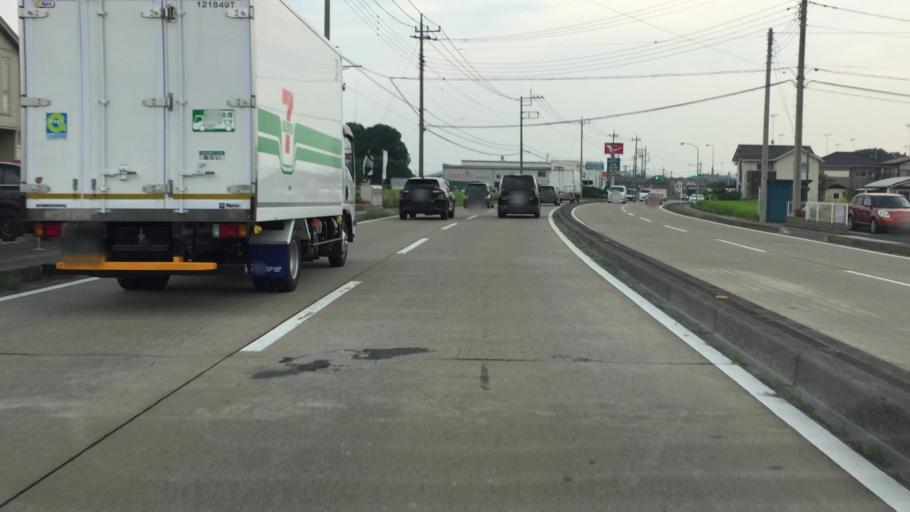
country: JP
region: Tochigi
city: Tochigi
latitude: 36.3447
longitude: 139.7003
